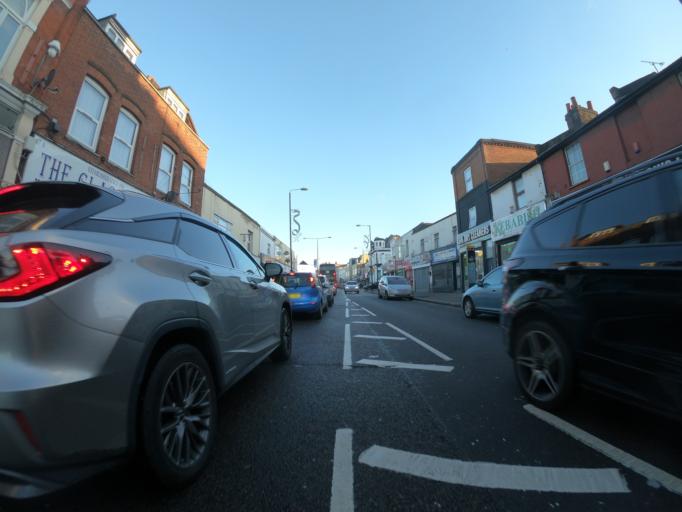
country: GB
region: England
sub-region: Greater London
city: Abbey Wood
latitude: 51.4883
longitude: 0.0899
